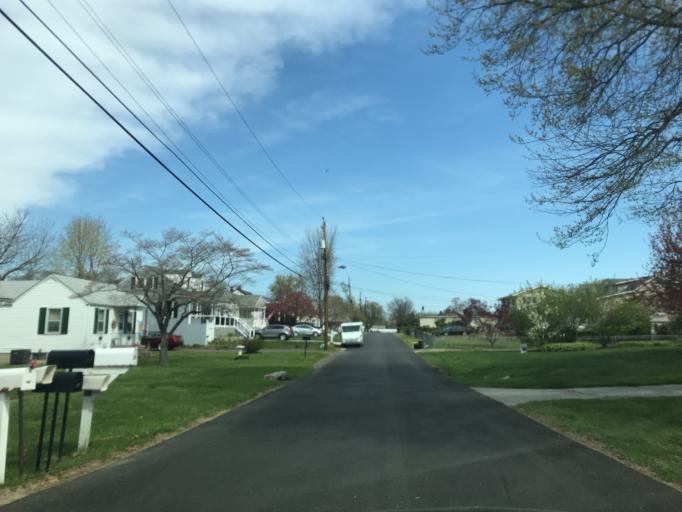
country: US
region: Maryland
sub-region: Baltimore County
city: Middle River
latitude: 39.3054
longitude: -76.4311
